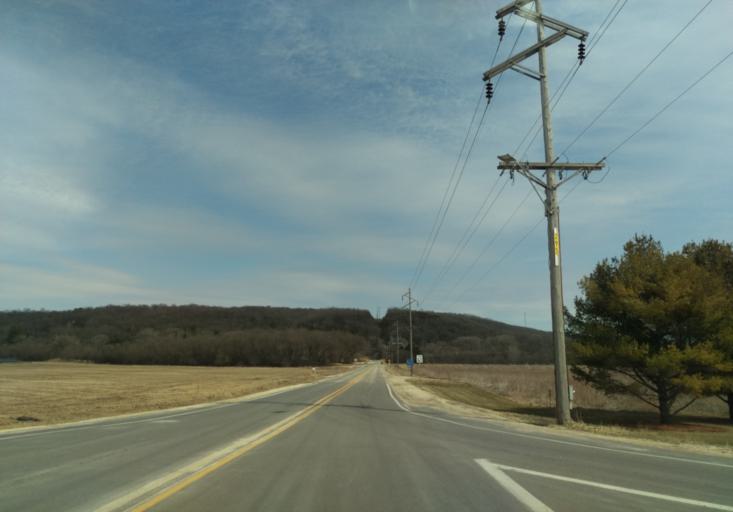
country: US
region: Iowa
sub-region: Winneshiek County
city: Decorah
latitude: 43.3204
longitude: -91.8137
